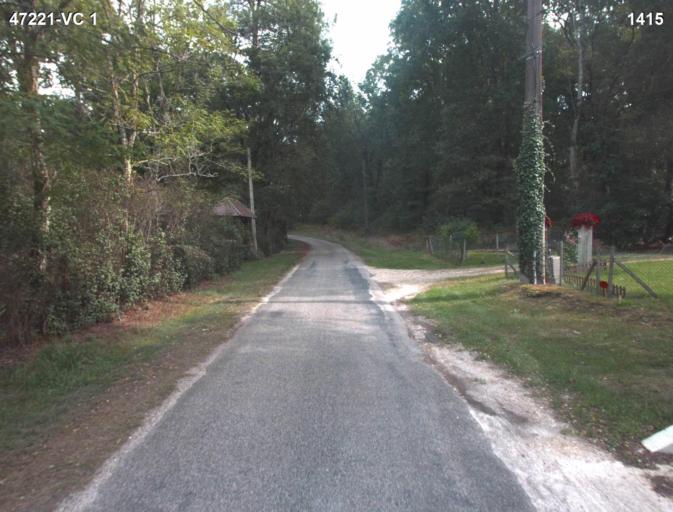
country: FR
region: Aquitaine
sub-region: Departement du Lot-et-Garonne
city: Mezin
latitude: 44.1101
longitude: 0.2338
